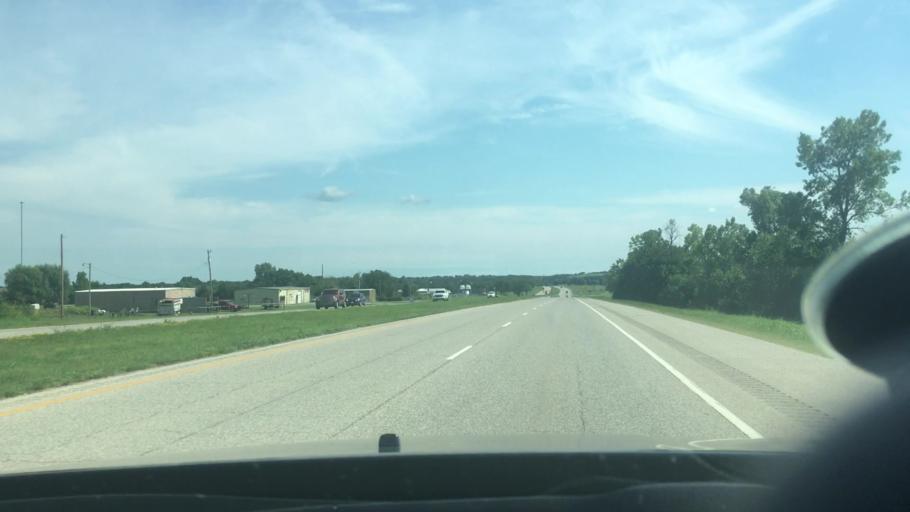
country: US
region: Oklahoma
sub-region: Seminole County
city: Seminole
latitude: 35.1951
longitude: -96.6752
